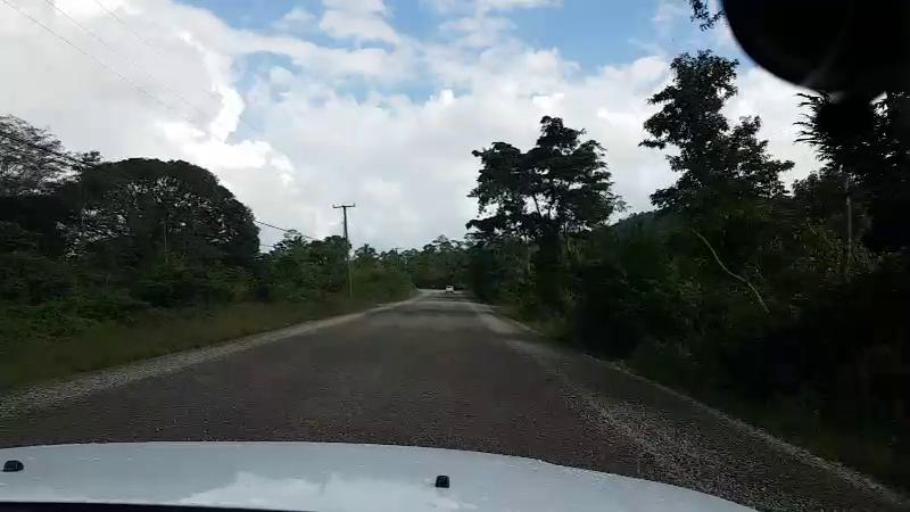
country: BZ
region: Cayo
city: Belmopan
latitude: 17.0891
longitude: -88.6190
